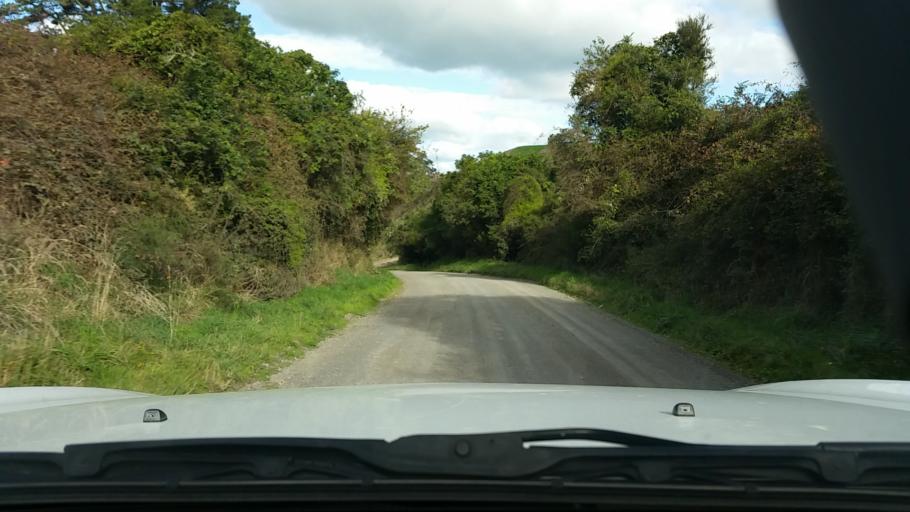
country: NZ
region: Waikato
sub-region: Taupo District
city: Taupo
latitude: -38.4850
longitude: 176.1859
